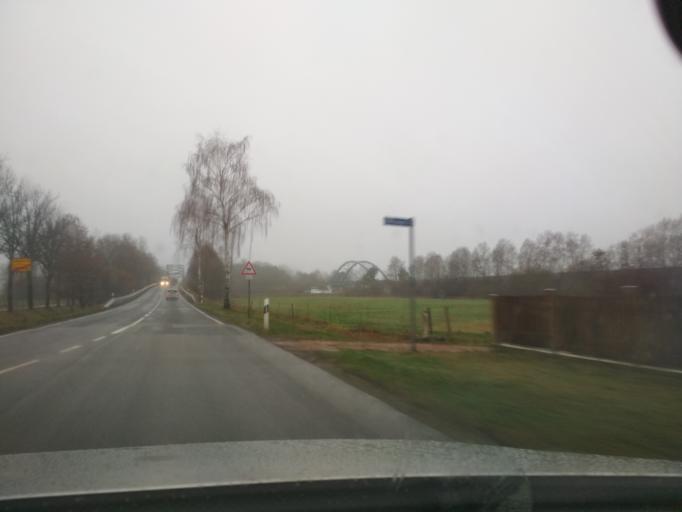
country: DE
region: Lower Saxony
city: Schoneworde
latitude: 52.6441
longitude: 10.6523
